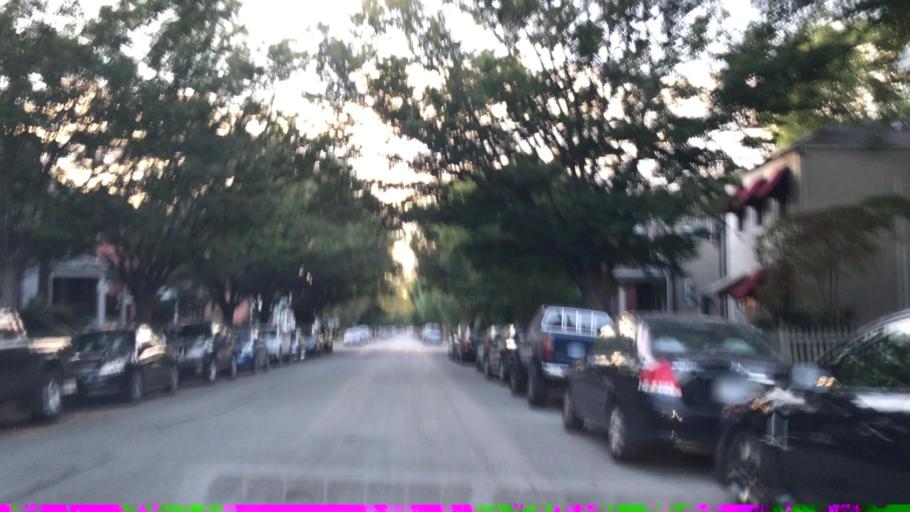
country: US
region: Virginia
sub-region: City of Richmond
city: Richmond
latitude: 37.5617
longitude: -77.4763
